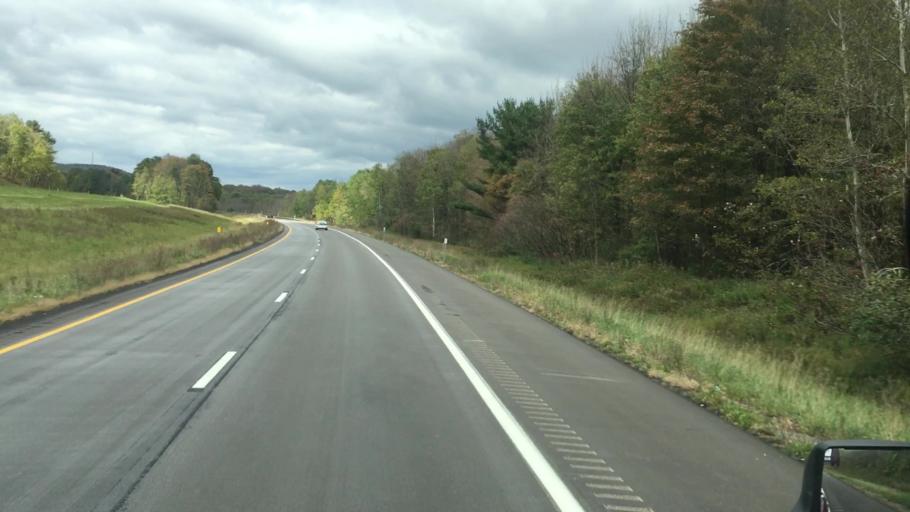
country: US
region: New York
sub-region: Cattaraugus County
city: Randolph
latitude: 42.1140
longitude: -78.9237
